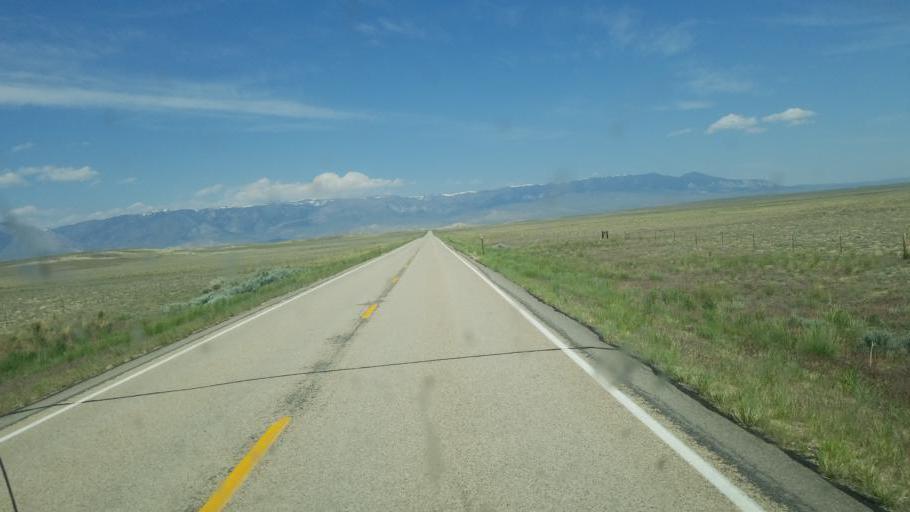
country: US
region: Wyoming
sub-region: Park County
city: Powell
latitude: 44.8633
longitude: -109.0320
